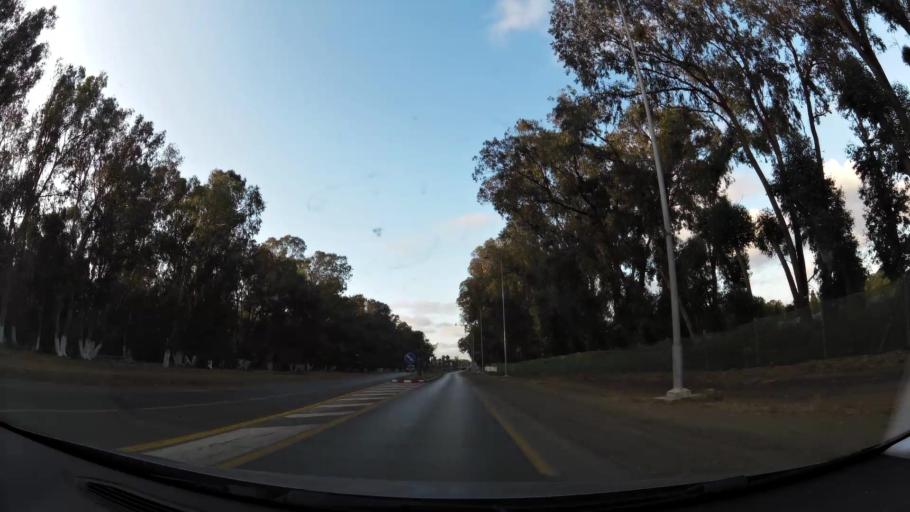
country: MA
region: Gharb-Chrarda-Beni Hssen
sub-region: Kenitra Province
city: Kenitra
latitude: 34.2005
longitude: -6.6783
